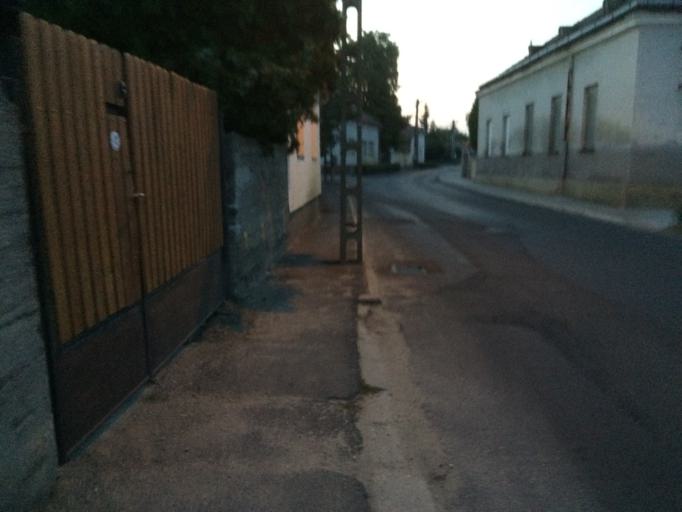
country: HU
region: Veszprem
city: Badacsonytomaj
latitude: 46.8054
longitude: 17.5140
